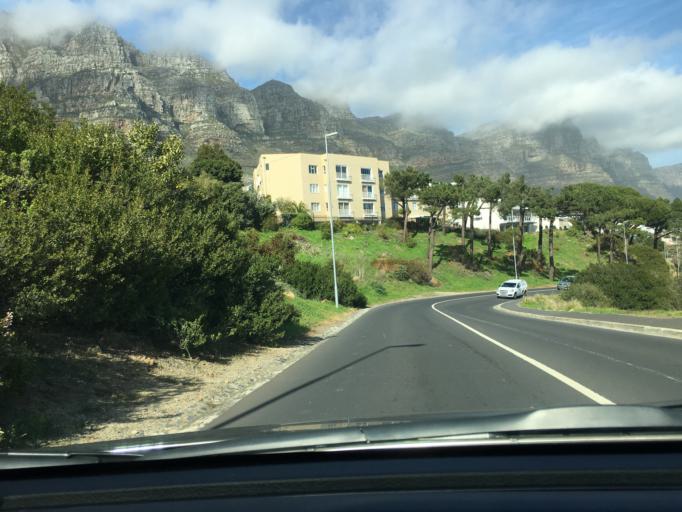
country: ZA
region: Western Cape
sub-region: City of Cape Town
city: Cape Town
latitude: -33.9540
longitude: 18.3862
